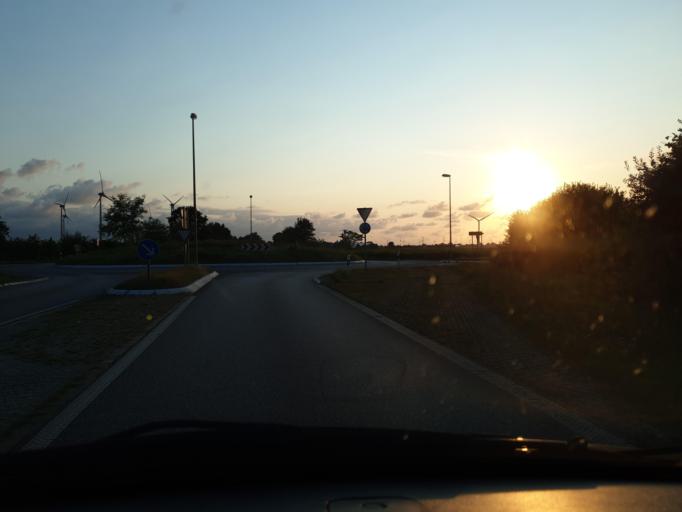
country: DE
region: Schleswig-Holstein
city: Brunsbuttel
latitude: 53.9066
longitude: 9.0907
